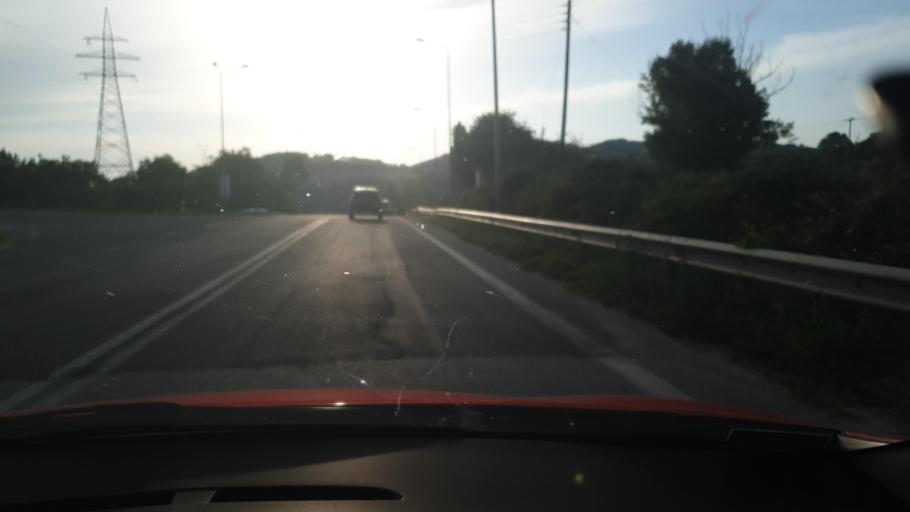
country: GR
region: Central Macedonia
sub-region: Nomos Chalkidikis
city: Galatista
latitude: 40.4620
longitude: 23.3280
